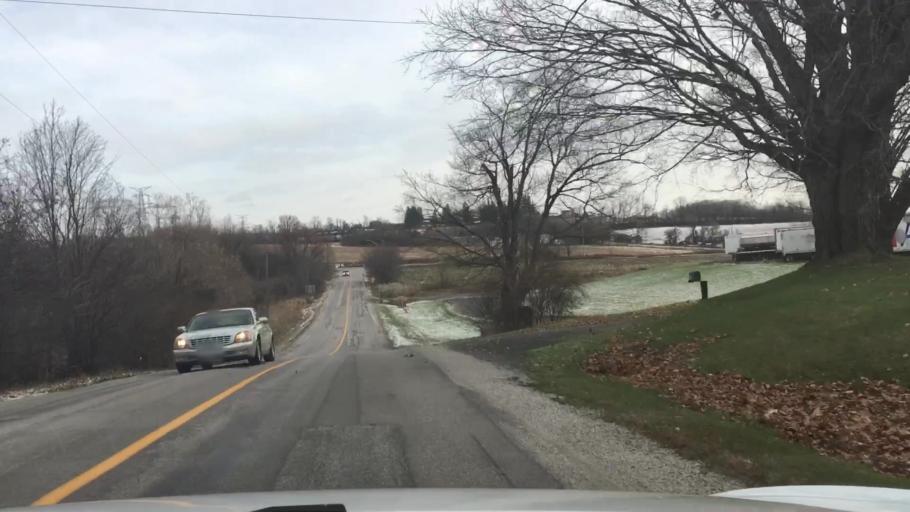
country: CA
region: Ontario
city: Oshawa
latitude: 43.9799
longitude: -78.8500
